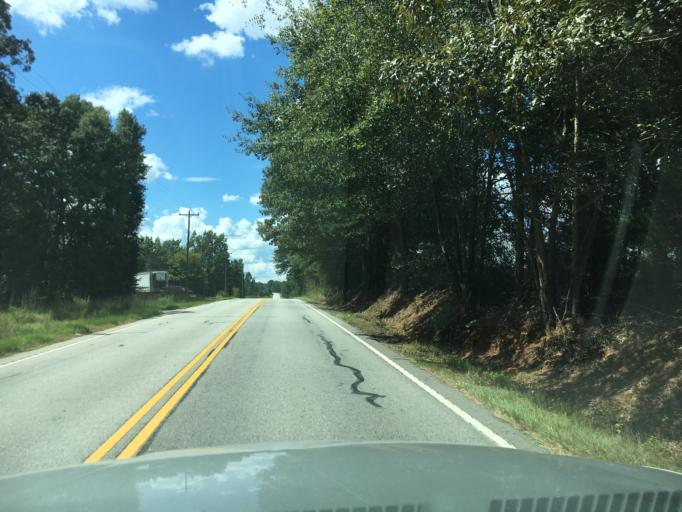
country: US
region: South Carolina
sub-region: Greenwood County
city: Ware Shoals
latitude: 34.5203
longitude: -82.1709
